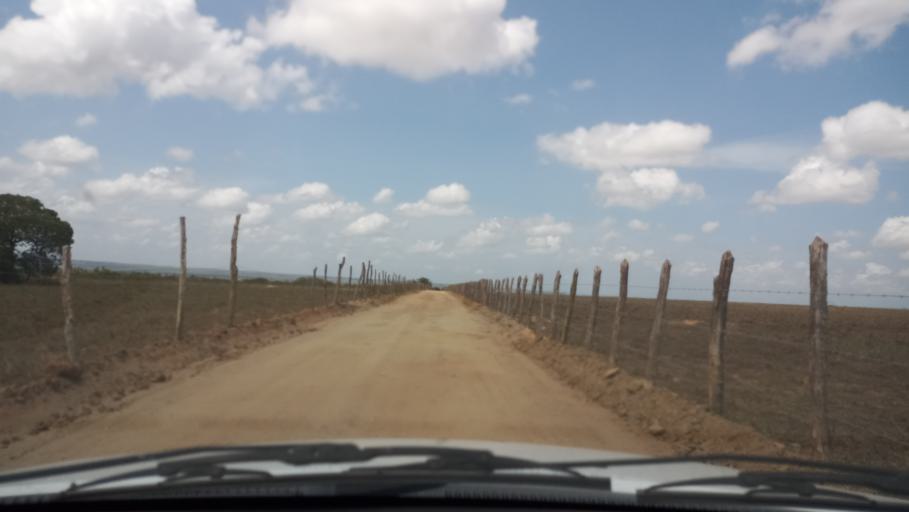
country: BR
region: Rio Grande do Norte
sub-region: Montanhas
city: Montanhas
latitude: -6.3535
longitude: -35.3346
